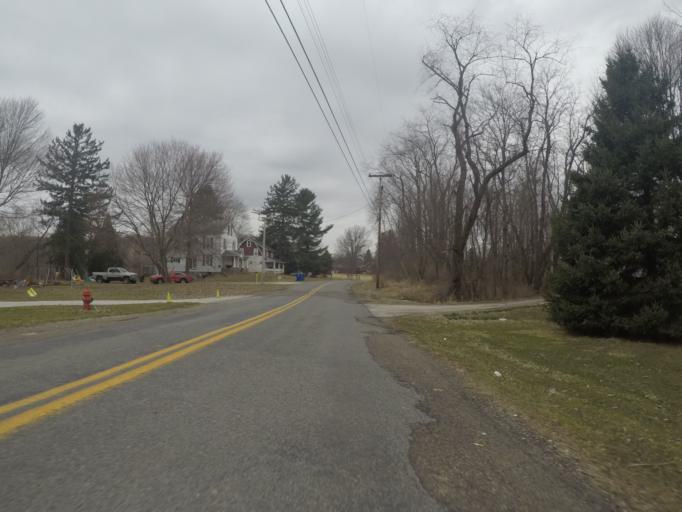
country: US
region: Ohio
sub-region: Portage County
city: Ravenna
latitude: 41.1740
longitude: -81.2909
